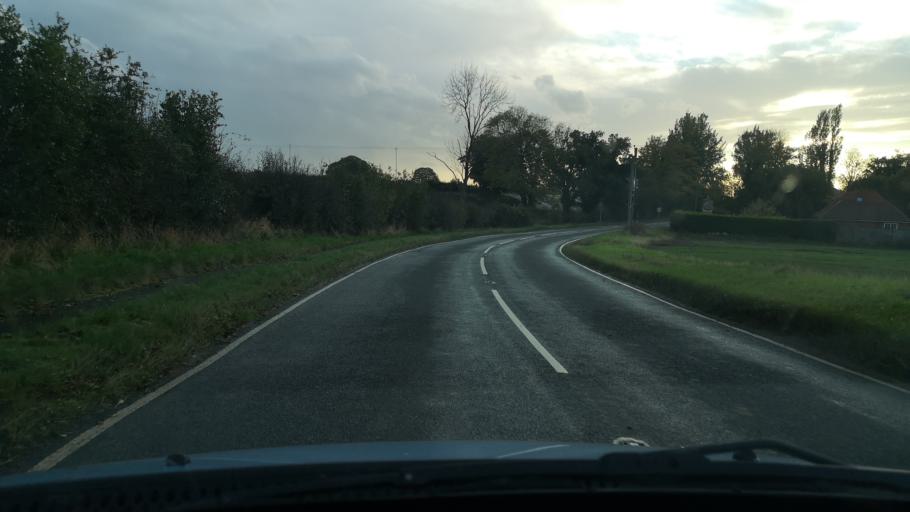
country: GB
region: England
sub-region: City and Borough of Wakefield
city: Badsworth
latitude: 53.6424
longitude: -1.2747
